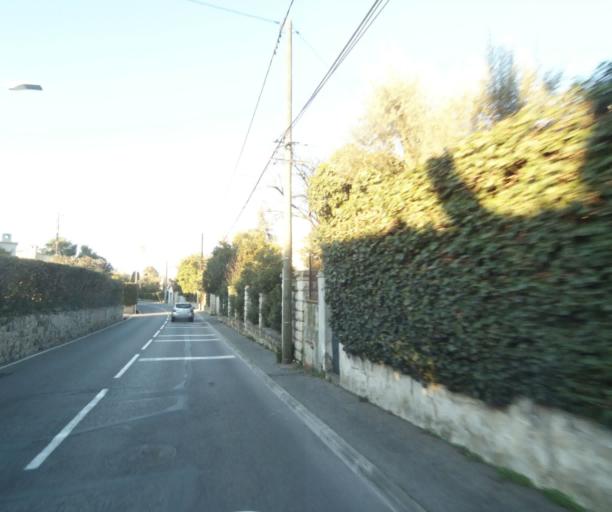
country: FR
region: Provence-Alpes-Cote d'Azur
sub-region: Departement des Alpes-Maritimes
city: Antibes
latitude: 43.5663
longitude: 7.1249
